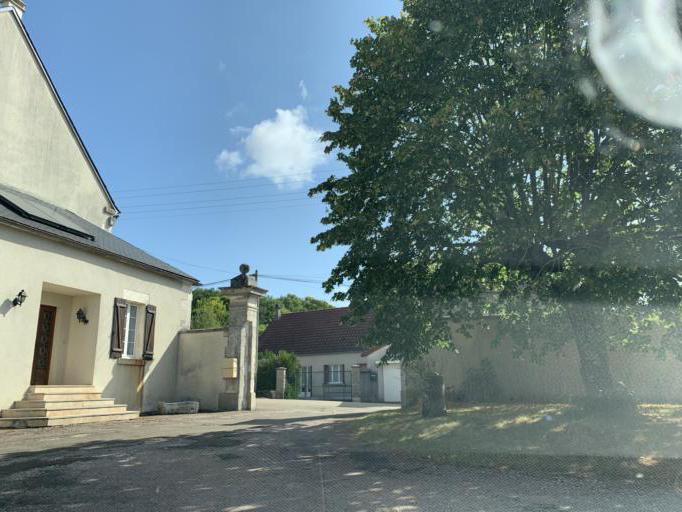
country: FR
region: Bourgogne
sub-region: Departement de l'Yonne
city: Fontenailles
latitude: 47.6174
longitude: 3.4993
